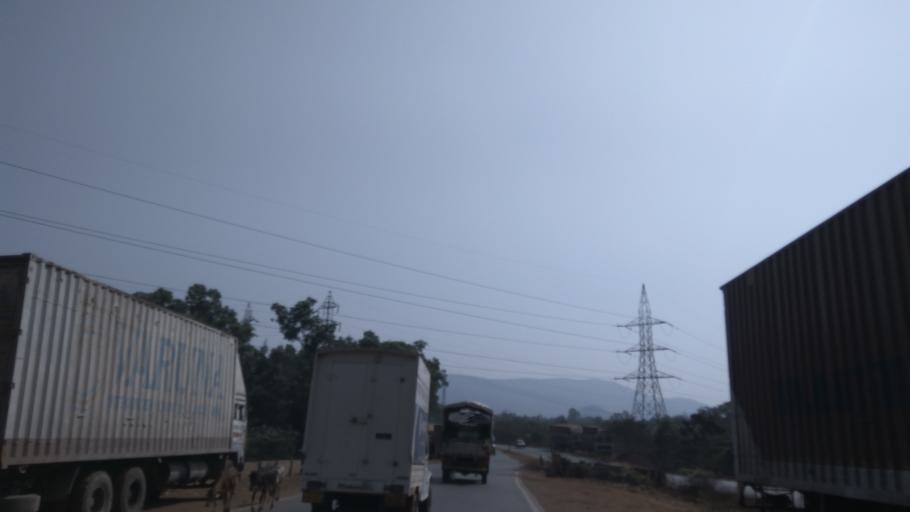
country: IN
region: Goa
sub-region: North Goa
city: Palle
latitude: 15.4165
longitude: 74.0716
